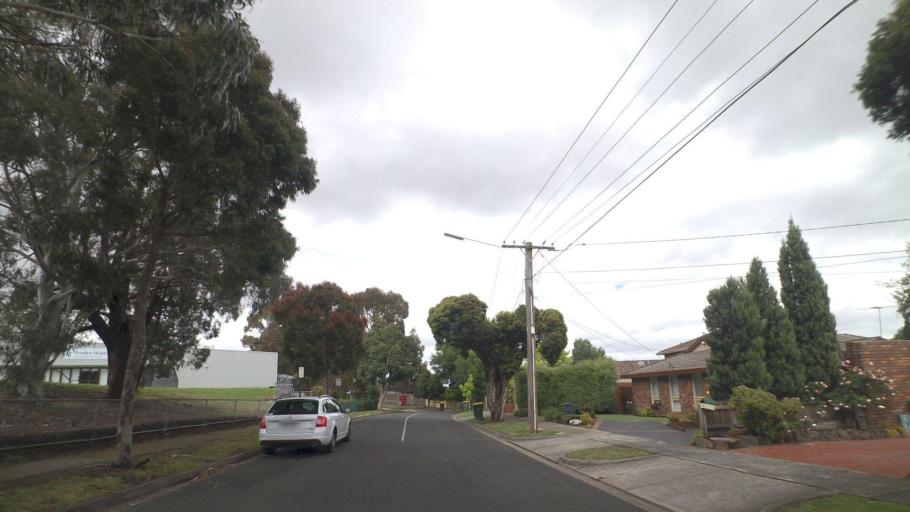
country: AU
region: Victoria
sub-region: Whitehorse
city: Vermont South
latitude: -37.8577
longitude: 145.1773
